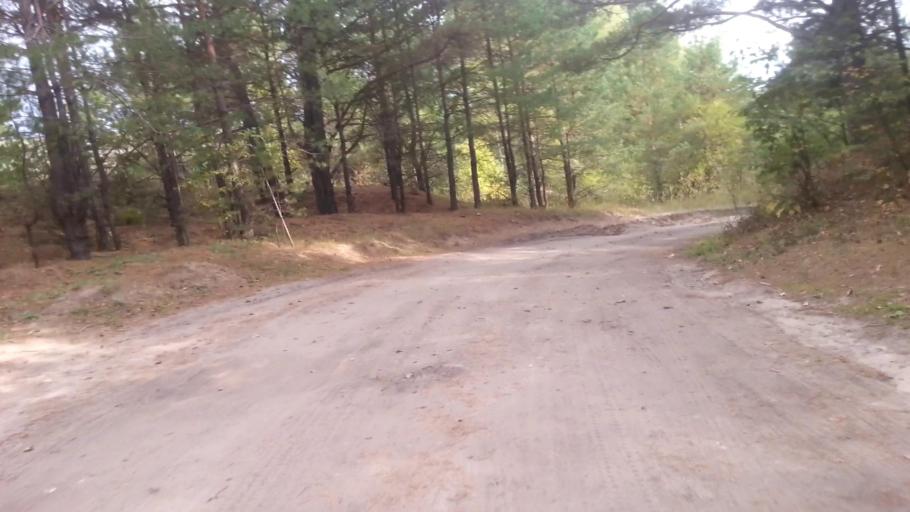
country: RU
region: Altai Krai
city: Yuzhnyy
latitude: 53.3088
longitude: 83.6996
